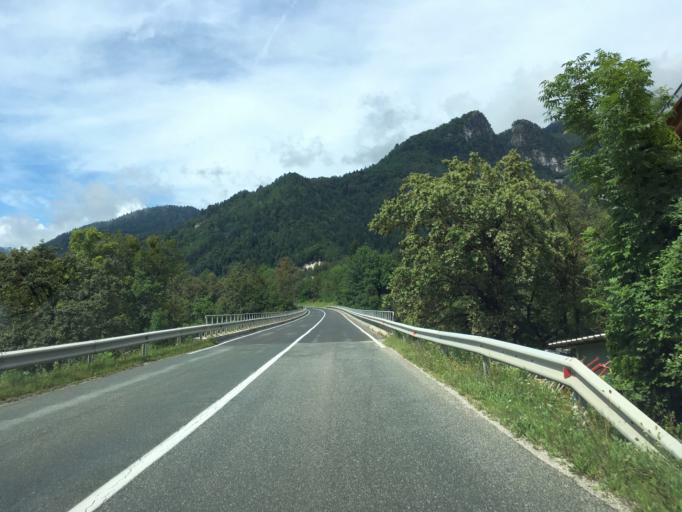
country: SI
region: Zirovnica
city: Zirovnica
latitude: 46.4083
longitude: 14.1309
